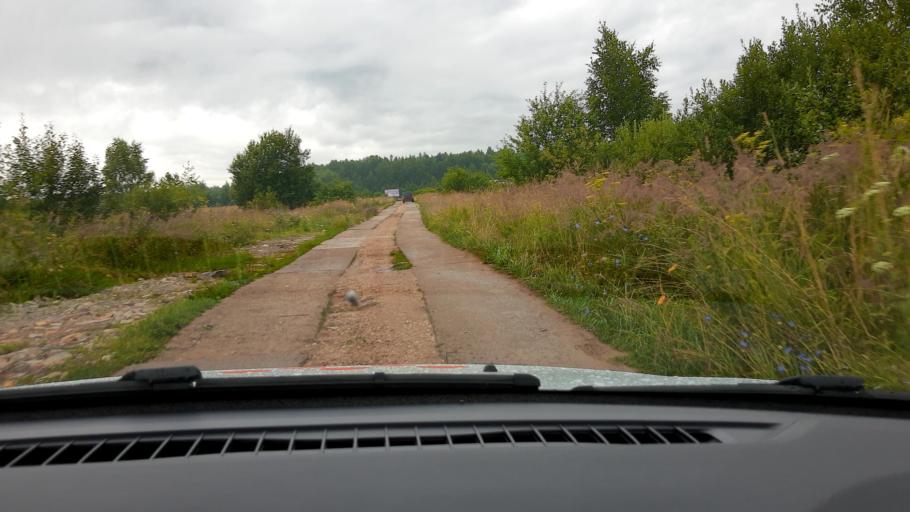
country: RU
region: Nizjnij Novgorod
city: Surovatikha
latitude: 55.9428
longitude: 43.9162
